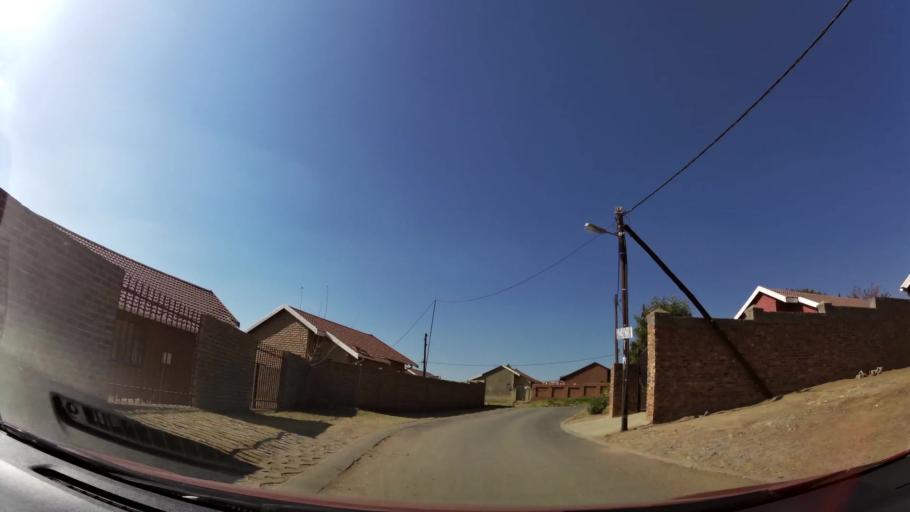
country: ZA
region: Gauteng
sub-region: West Rand District Municipality
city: Muldersdriseloop
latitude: -26.0136
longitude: 27.9349
